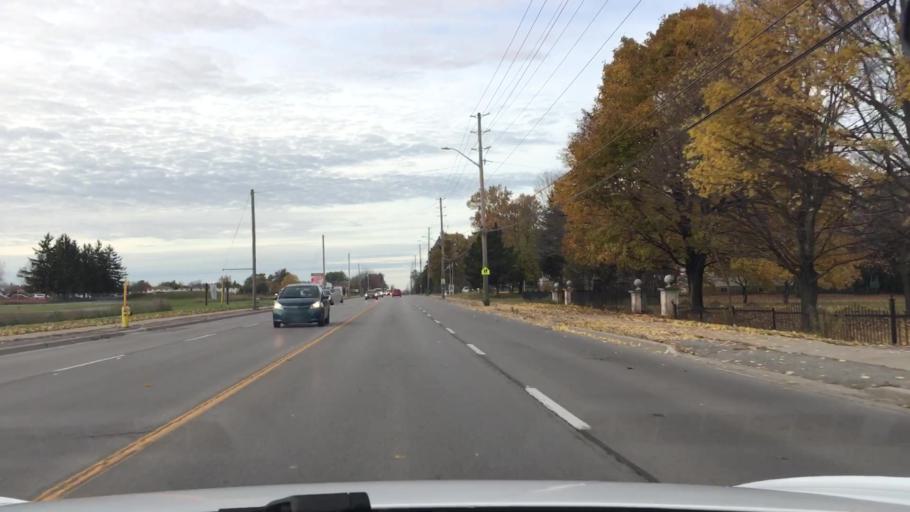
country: CA
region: Ontario
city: Oshawa
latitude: 43.9107
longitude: -78.8152
